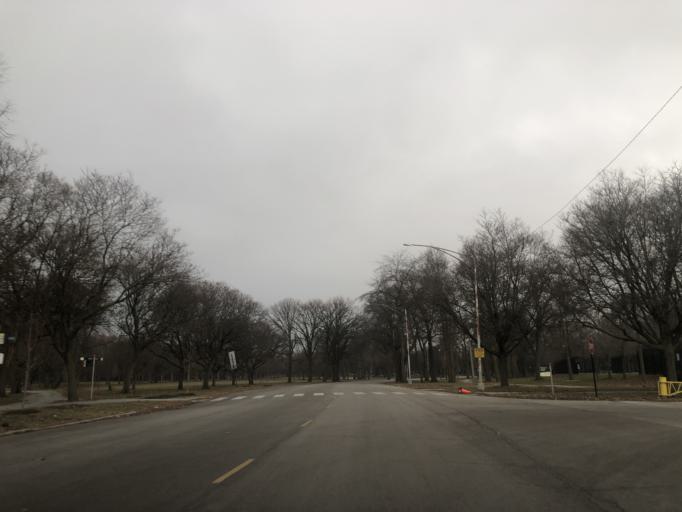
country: US
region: Illinois
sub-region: Cook County
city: Chicago
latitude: 41.7932
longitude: -87.6134
